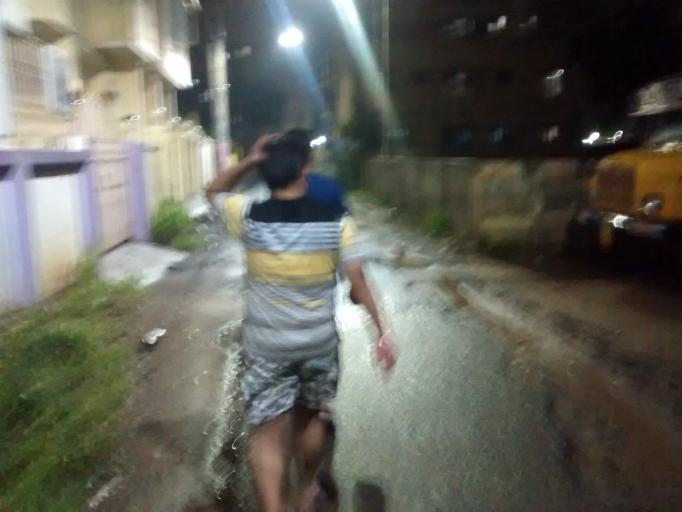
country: IN
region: Tamil Nadu
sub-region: Kancheepuram
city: Perungudi
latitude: 12.9461
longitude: 80.2363
